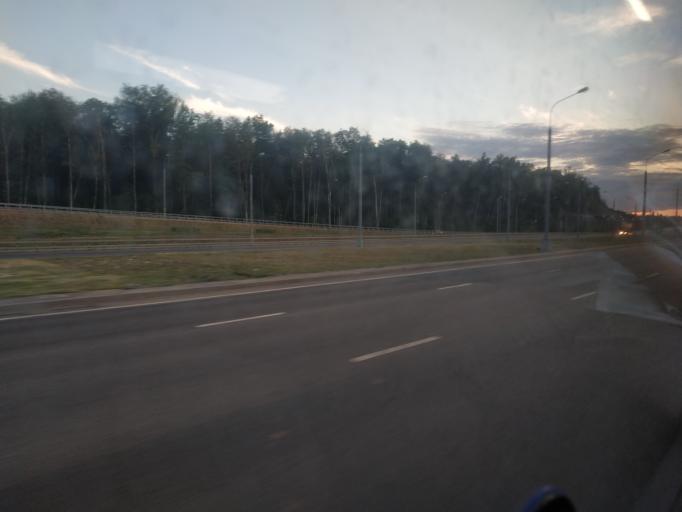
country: RU
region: Moscow
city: Solntsevo
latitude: 55.6091
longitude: 37.3930
